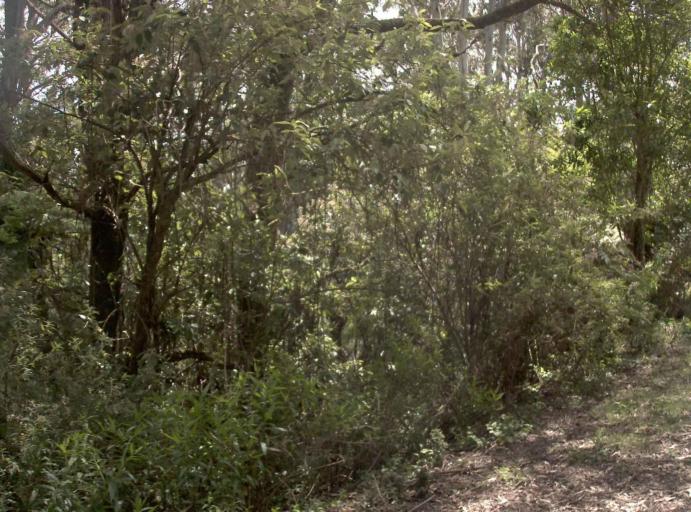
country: AU
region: Victoria
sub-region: Latrobe
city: Morwell
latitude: -38.4346
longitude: 146.5274
